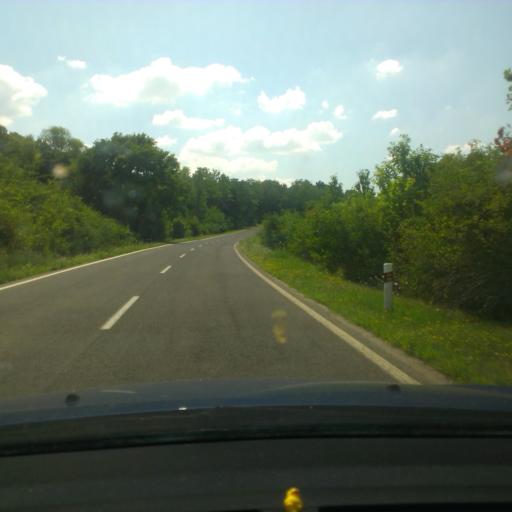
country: SK
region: Trnavsky
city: Hlohovec
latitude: 48.4913
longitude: 17.8135
